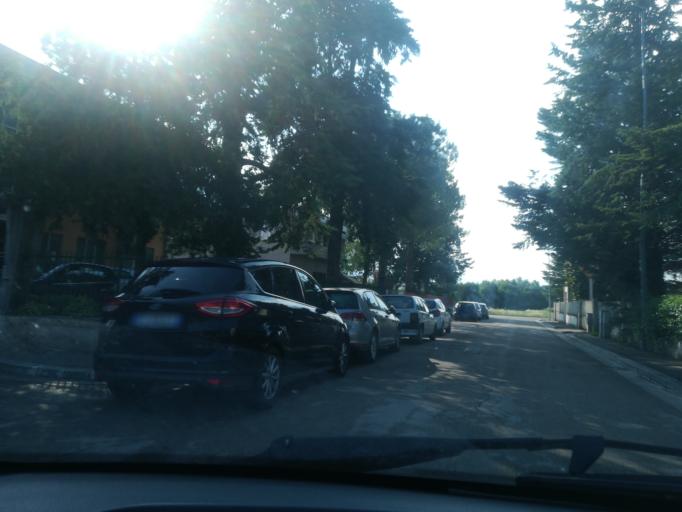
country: IT
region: The Marches
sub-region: Provincia di Macerata
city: Villa Potenza
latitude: 43.3171
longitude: 13.4204
